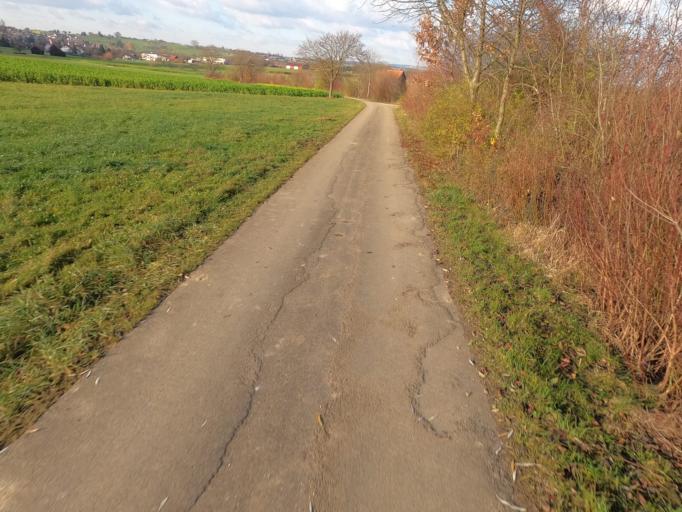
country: DE
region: Baden-Wuerttemberg
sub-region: Regierungsbezirk Stuttgart
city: Hattenhofen
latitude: 48.6652
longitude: 9.5900
